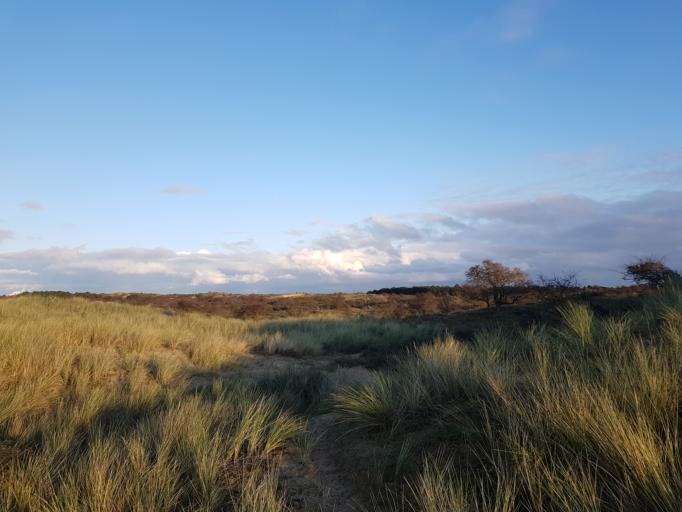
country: NL
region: South Holland
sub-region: Gemeente Noordwijkerhout
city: Noordwijkerhout
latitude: 52.3188
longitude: 4.5013
